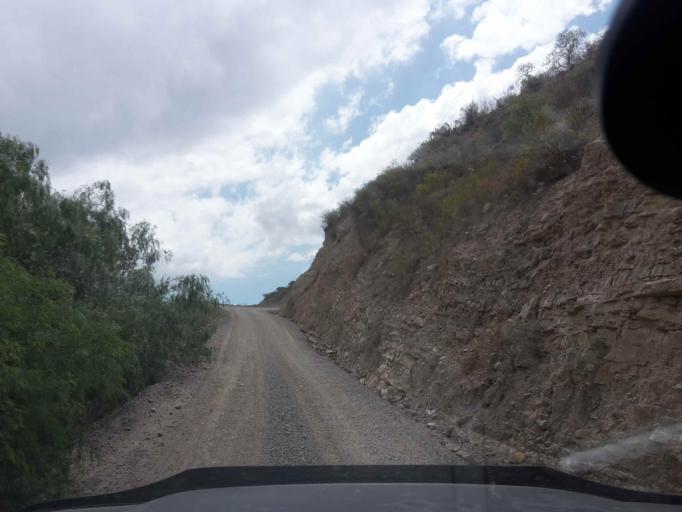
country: BO
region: Cochabamba
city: Sipe Sipe
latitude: -17.5525
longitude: -66.4756
